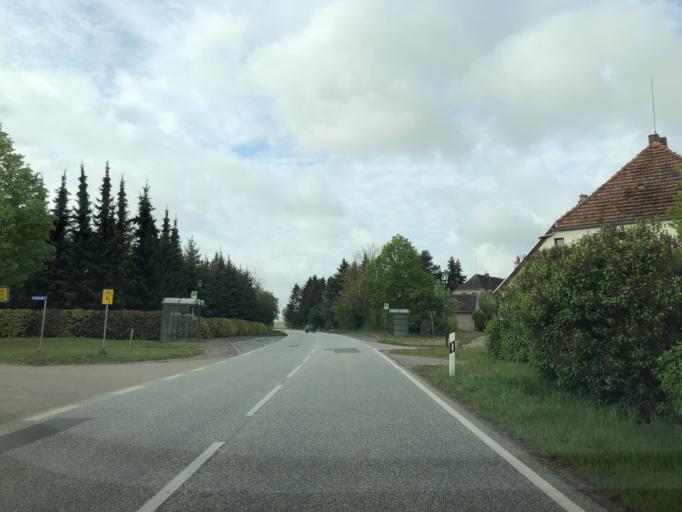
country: DE
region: Mecklenburg-Vorpommern
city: Goldberg
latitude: 53.5755
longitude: 12.0795
